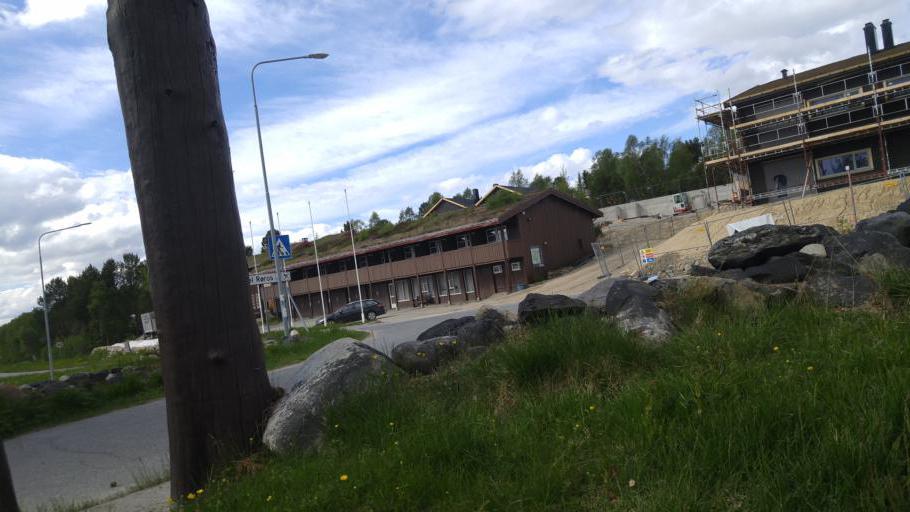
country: NO
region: Sor-Trondelag
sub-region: Roros
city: Roros
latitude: 62.5799
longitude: 11.3791
